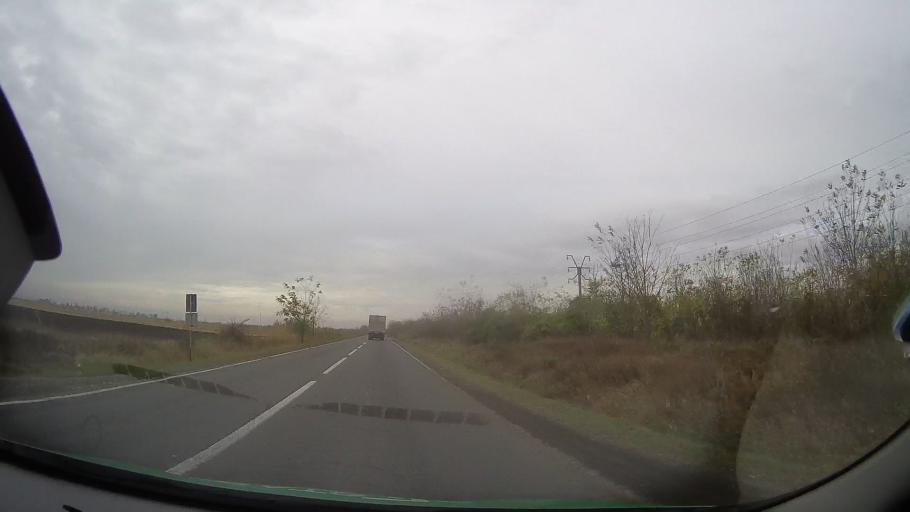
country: RO
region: Prahova
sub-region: Oras Urlati
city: Urlati
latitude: 44.9588
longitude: 26.2509
